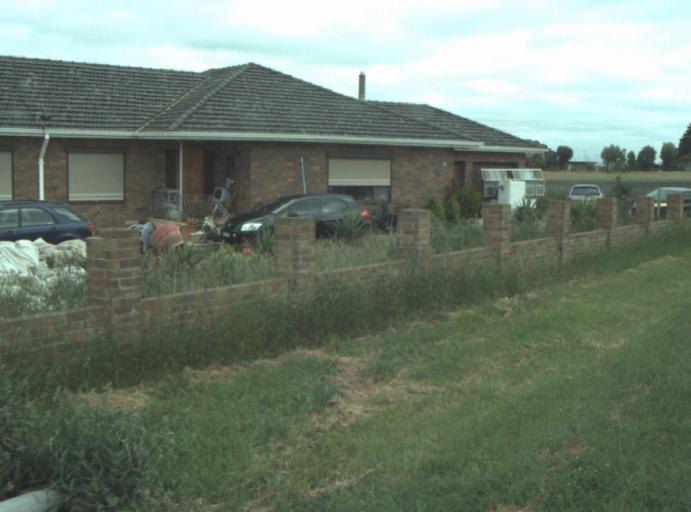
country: AU
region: Victoria
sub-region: Greater Geelong
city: Bell Post Hill
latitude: -38.0601
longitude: 144.3219
